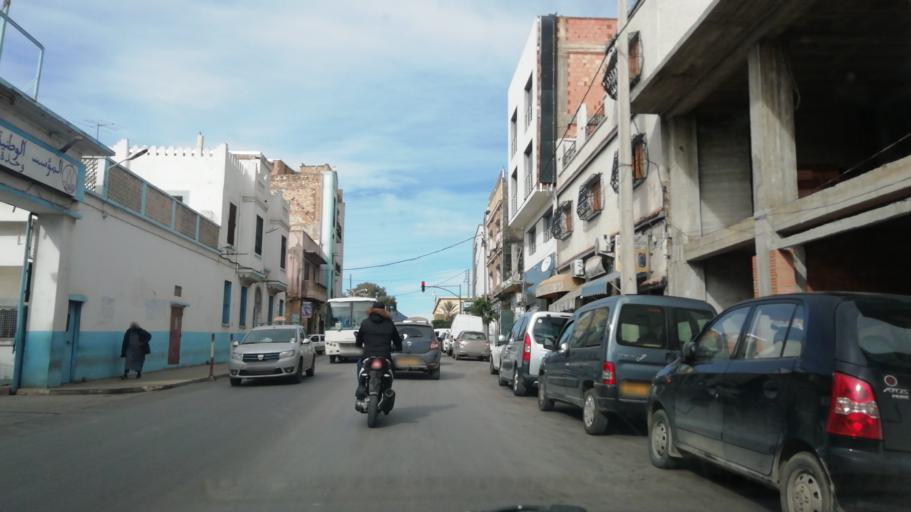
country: DZ
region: Oran
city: Oran
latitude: 35.6933
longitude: -0.6310
